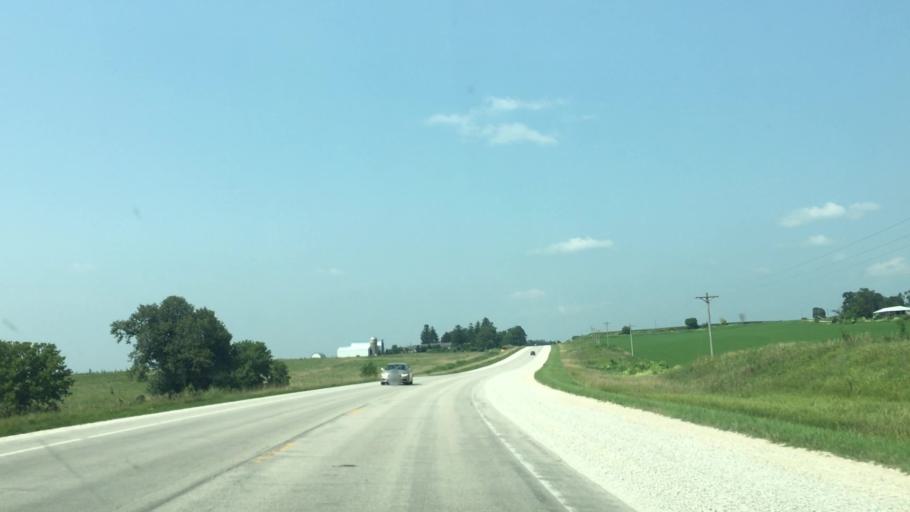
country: US
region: Iowa
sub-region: Winneshiek County
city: Decorah
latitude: 43.4150
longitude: -91.8591
